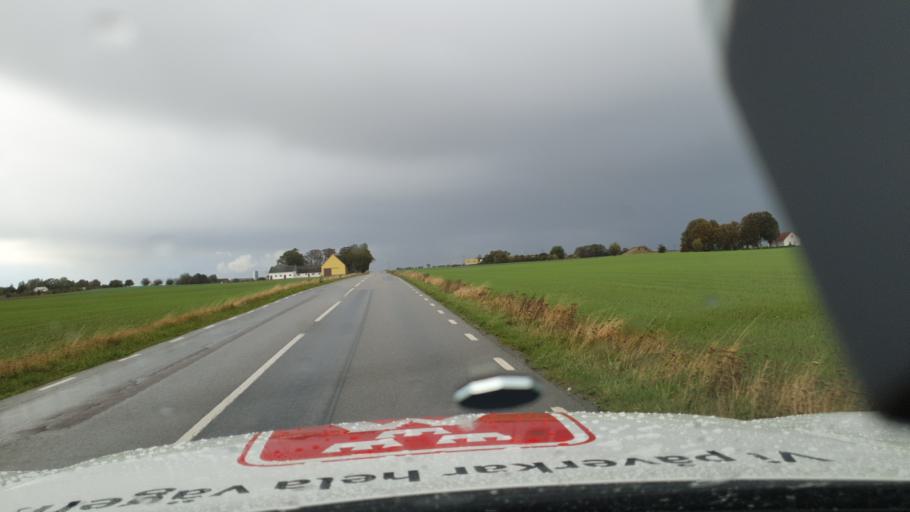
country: SE
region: Skane
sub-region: Malmo
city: Tygelsjo
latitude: 55.5094
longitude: 13.0233
